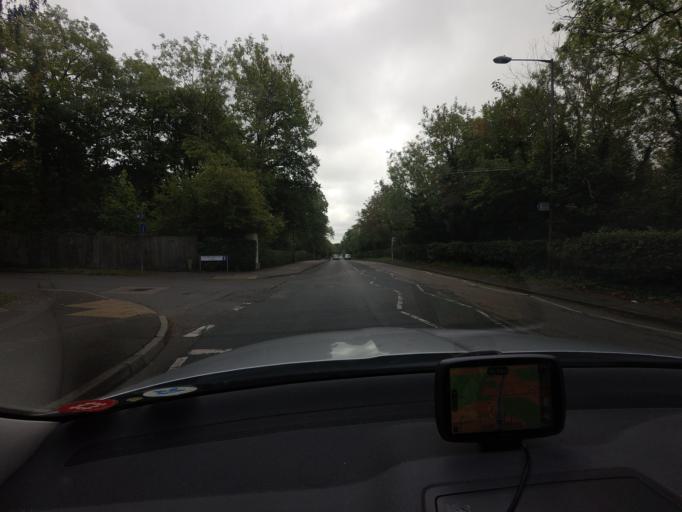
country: GB
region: England
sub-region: Kent
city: Tonbridge
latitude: 51.2147
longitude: 0.2460
